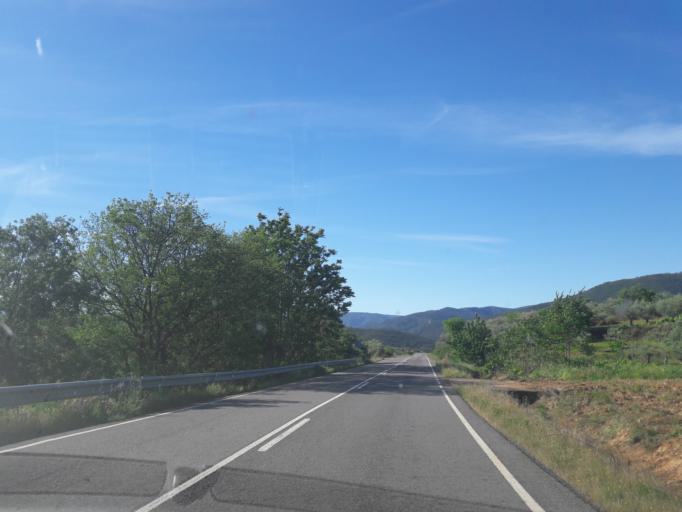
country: ES
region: Castille and Leon
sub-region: Provincia de Salamanca
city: Sotoserrano
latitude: 40.4294
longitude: -6.0332
